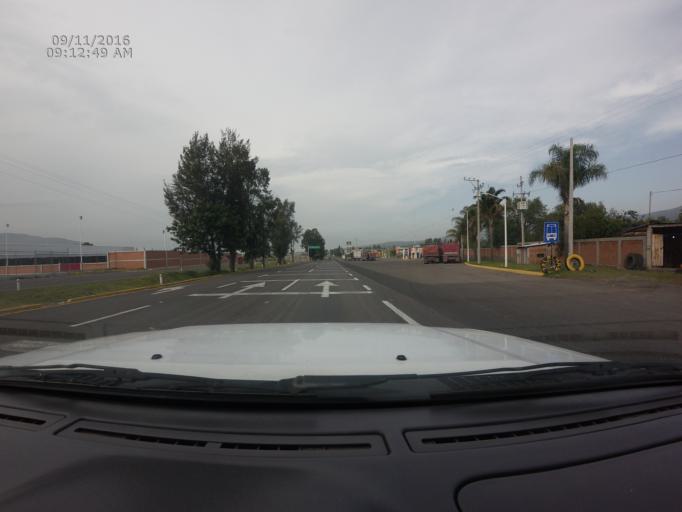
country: MX
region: Michoacan
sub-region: Morelia
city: La Mintzita (Piedra Dura)
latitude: 19.5881
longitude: -101.3024
